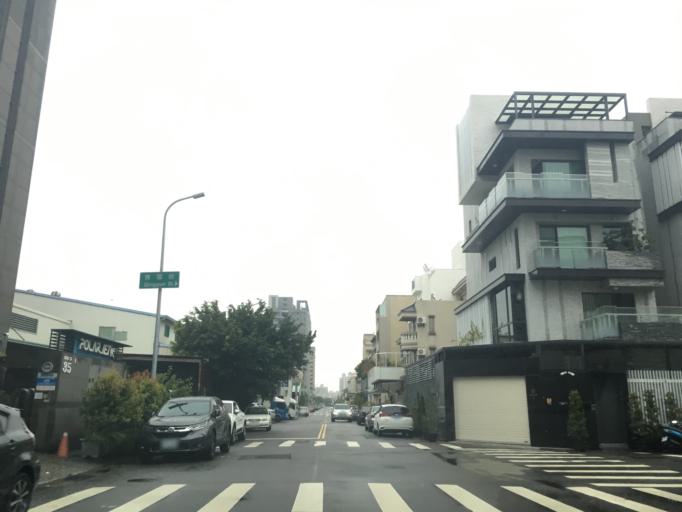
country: TW
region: Taiwan
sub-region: Taichung City
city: Taichung
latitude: 24.1654
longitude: 120.7110
